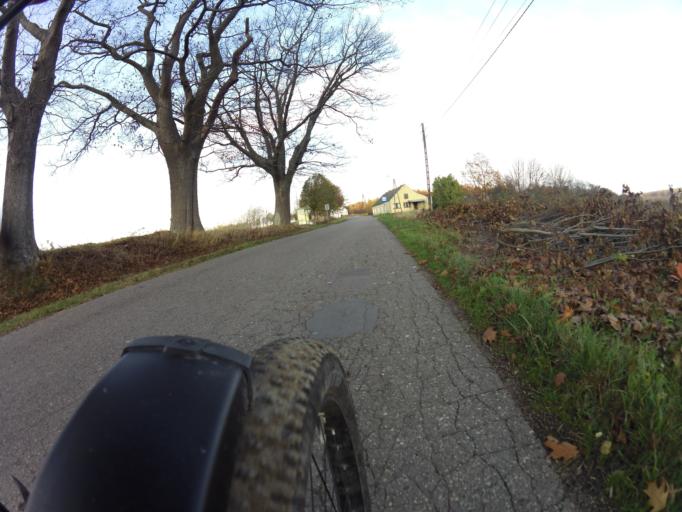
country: PL
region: Pomeranian Voivodeship
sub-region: Powiat pucki
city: Krokowa
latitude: 54.7532
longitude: 18.1839
